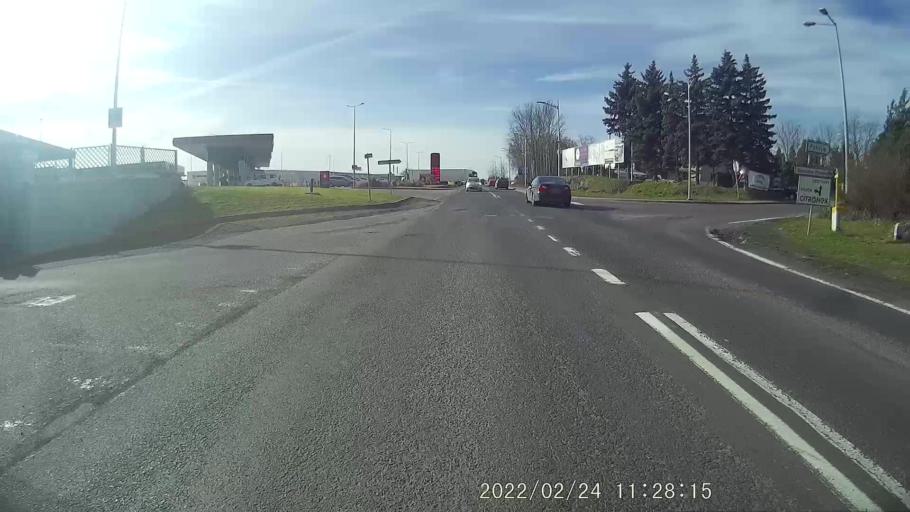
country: PL
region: Lower Silesian Voivodeship
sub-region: Powiat polkowicki
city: Przemkow
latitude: 51.5333
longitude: 15.6799
